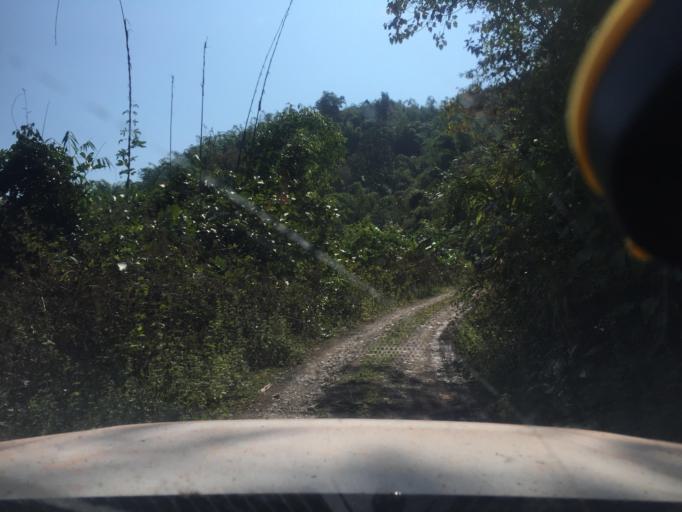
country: LA
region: Phongsali
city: Phongsali
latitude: 21.7048
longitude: 102.4009
